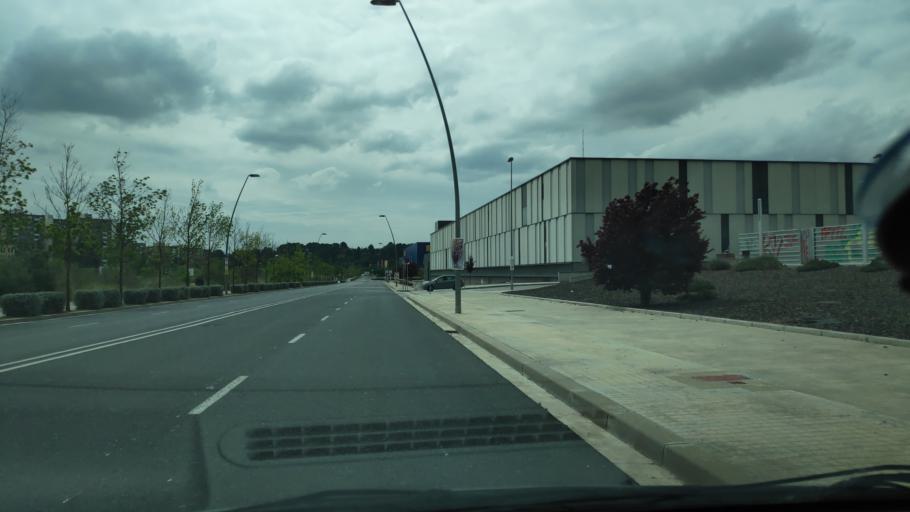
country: ES
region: Catalonia
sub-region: Provincia de Barcelona
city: Barbera del Valles
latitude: 41.5135
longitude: 2.1085
